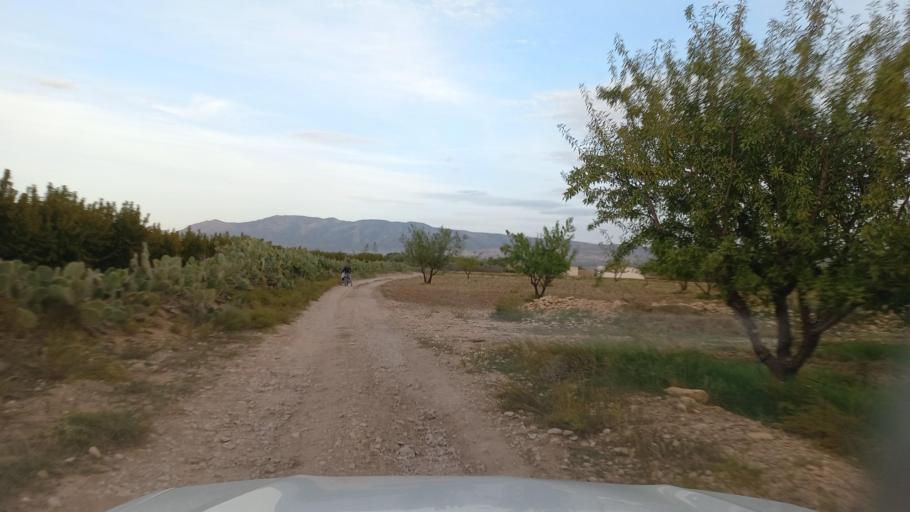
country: TN
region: Al Qasrayn
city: Sbiba
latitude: 35.4229
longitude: 9.1004
